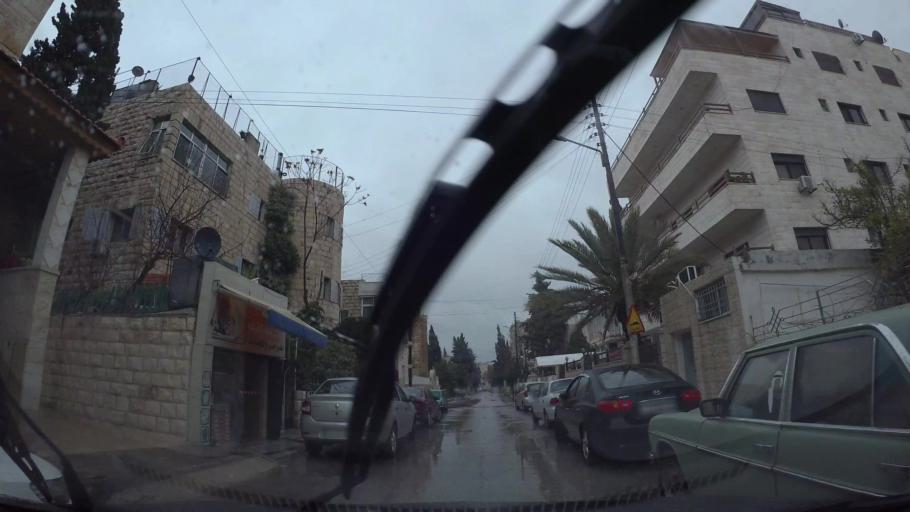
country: JO
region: Amman
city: Amman
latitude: 31.9574
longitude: 35.9163
